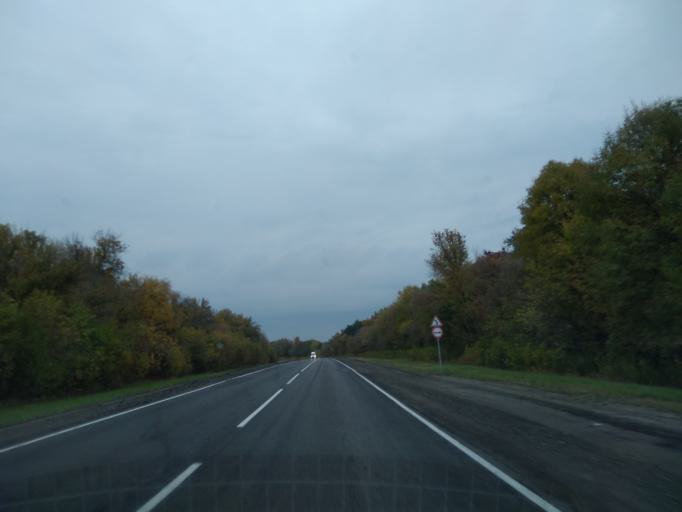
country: RU
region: Lipetsk
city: Zadonsk
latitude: 52.5153
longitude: 38.7579
